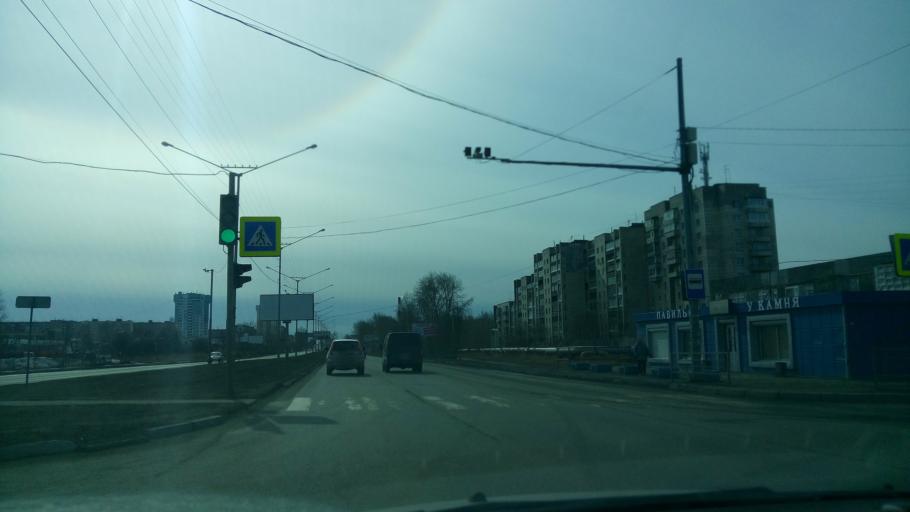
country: RU
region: Sverdlovsk
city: Nizhniy Tagil
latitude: 57.8899
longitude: 59.9407
